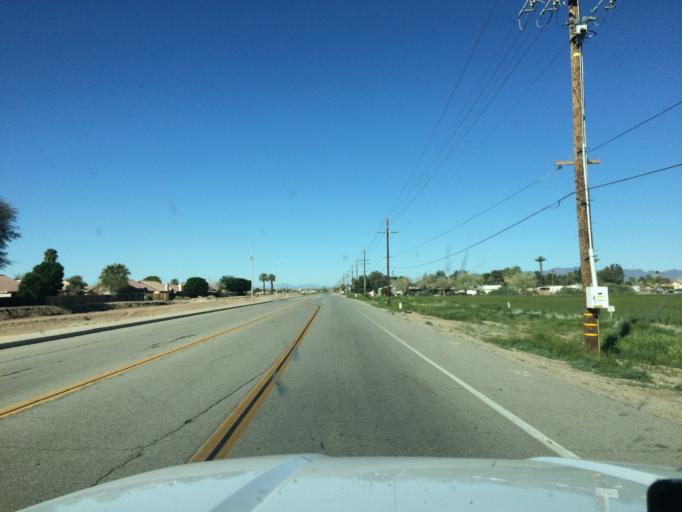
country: US
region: California
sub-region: Riverside County
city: Blythe
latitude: 33.6100
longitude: -114.6252
